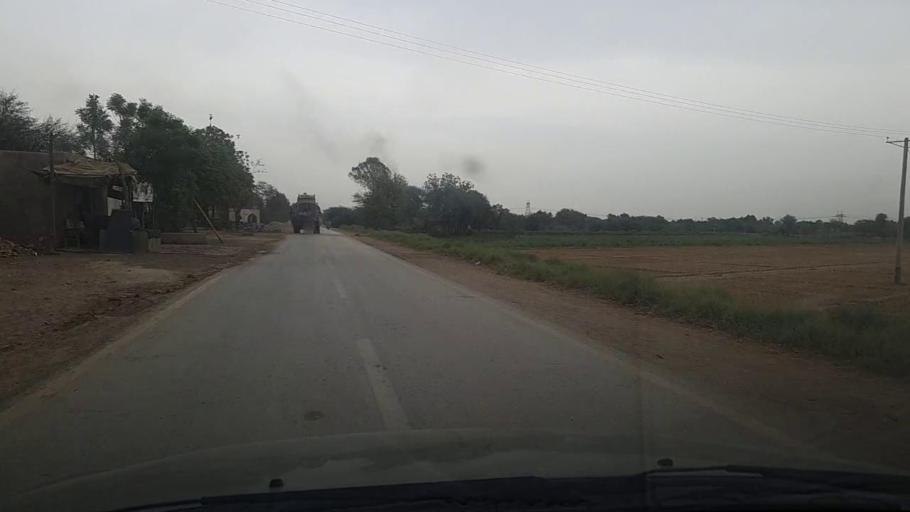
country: PK
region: Sindh
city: Daulatpur
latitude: 26.3387
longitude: 68.1213
